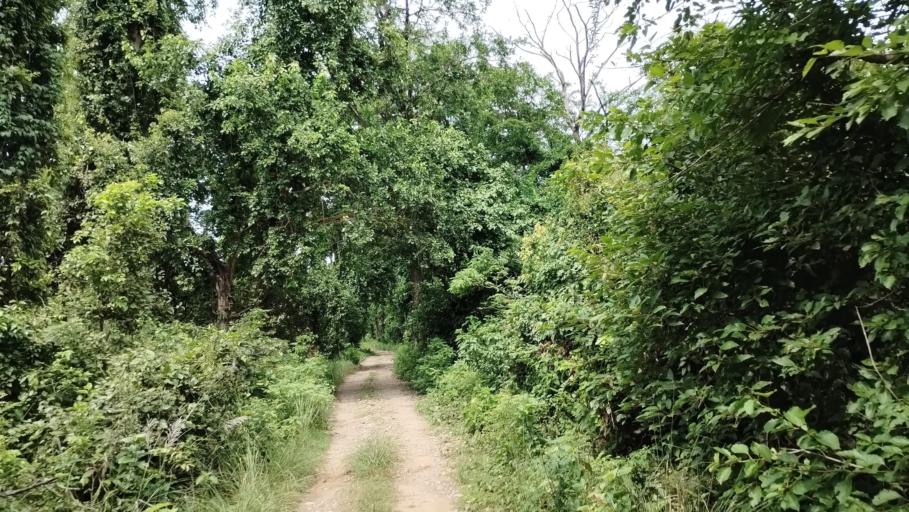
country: NP
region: Far Western
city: Tikapur
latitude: 28.4562
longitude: 81.2423
